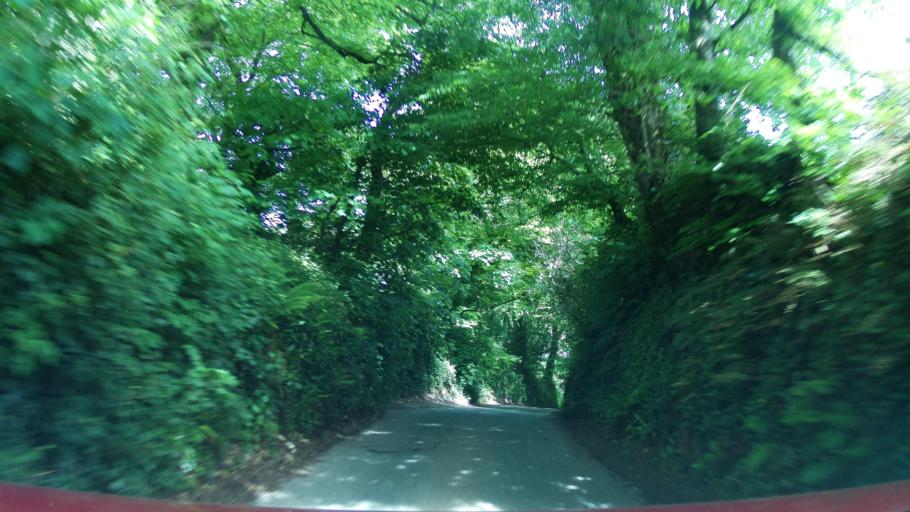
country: GB
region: England
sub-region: Devon
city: Totnes
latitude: 50.3641
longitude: -3.7257
